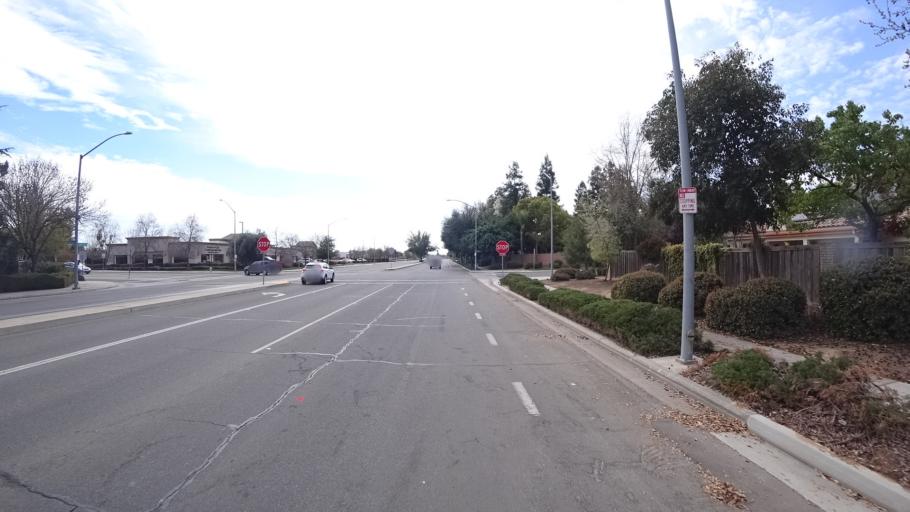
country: US
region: California
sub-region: Fresno County
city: West Park
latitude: 36.8410
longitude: -119.8792
